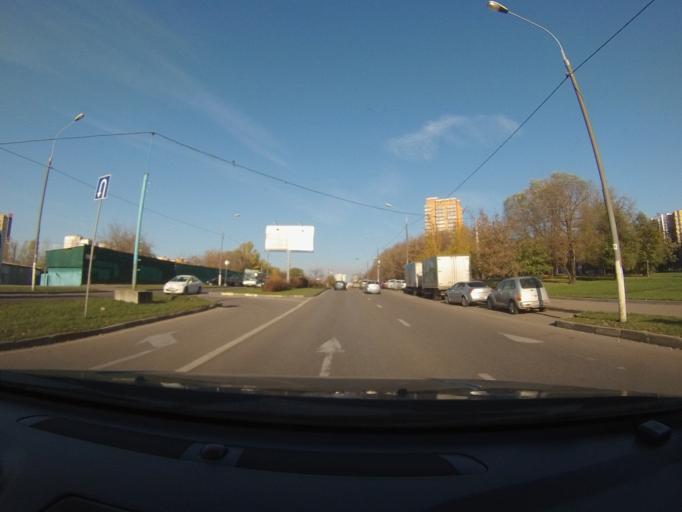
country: RU
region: Moscow
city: Golovinskiy
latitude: 55.8570
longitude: 37.4916
